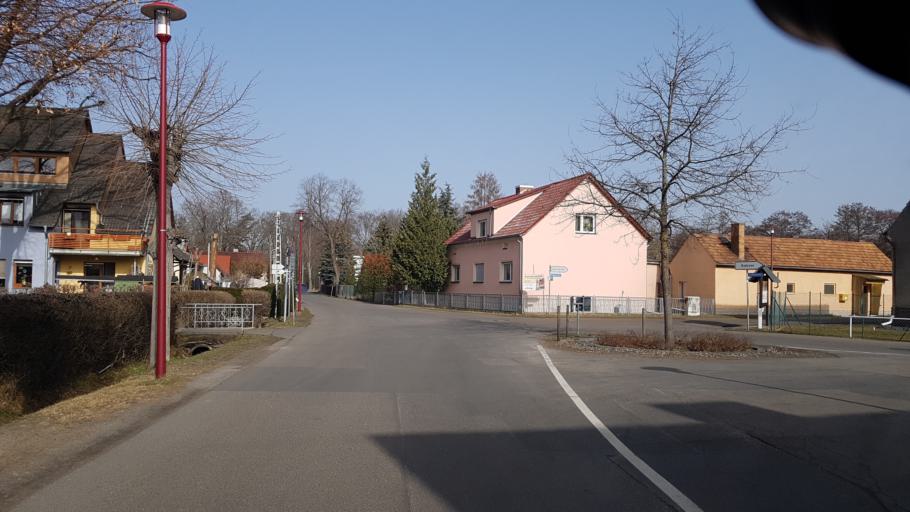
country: DE
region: Brandenburg
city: Cottbus
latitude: 51.7375
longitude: 14.3693
